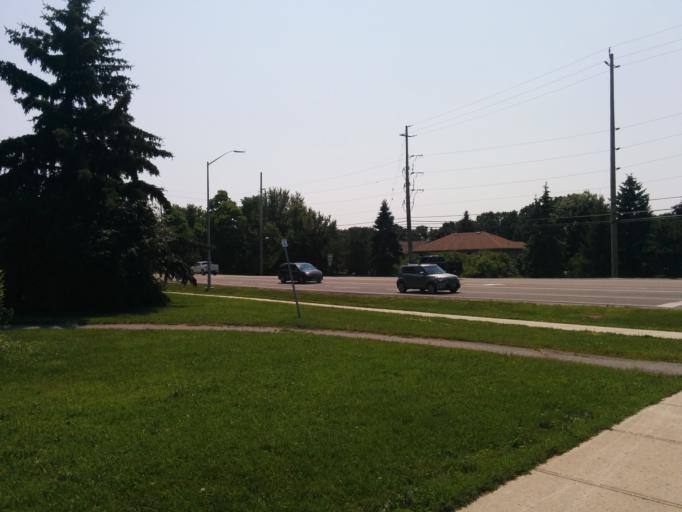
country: CA
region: Ontario
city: Kingston
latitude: 44.2590
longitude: -76.4602
